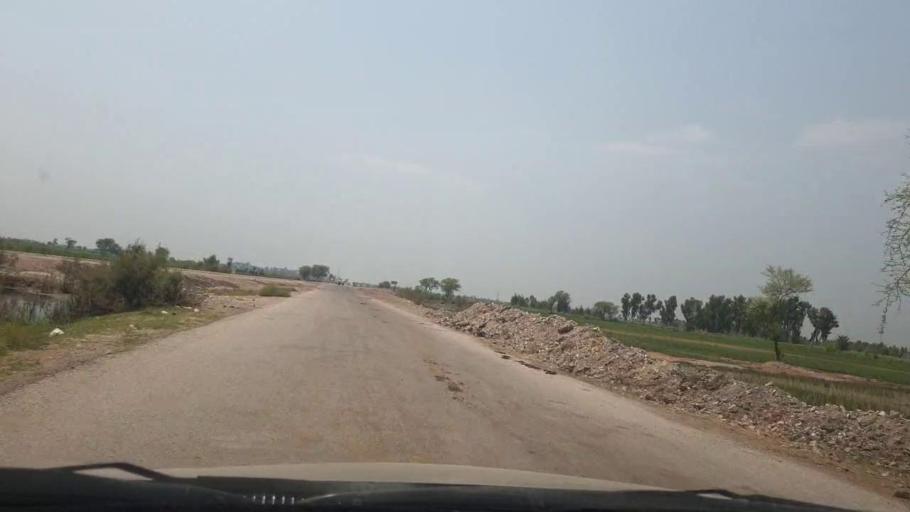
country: PK
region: Sindh
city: Ratodero
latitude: 27.7152
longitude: 68.2771
